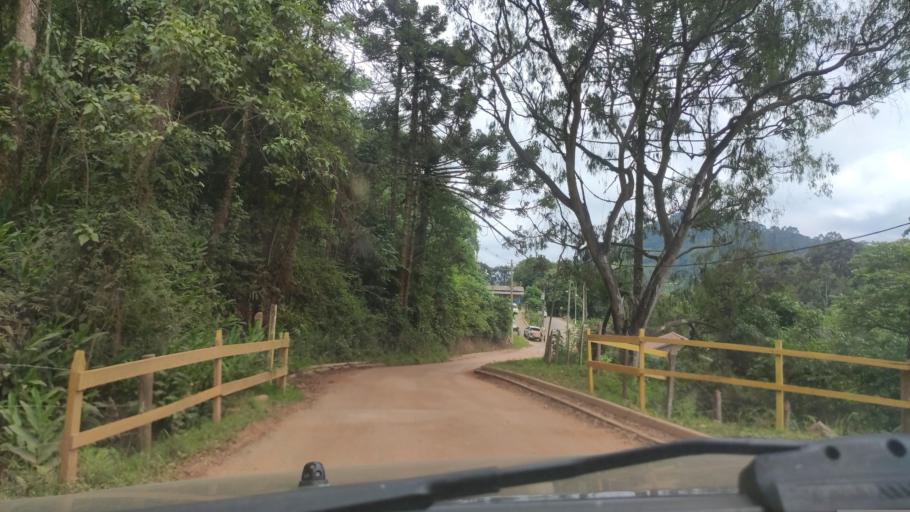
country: BR
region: Minas Gerais
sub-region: Paraisopolis
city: Paraisopolis
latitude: -22.6655
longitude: -45.8535
